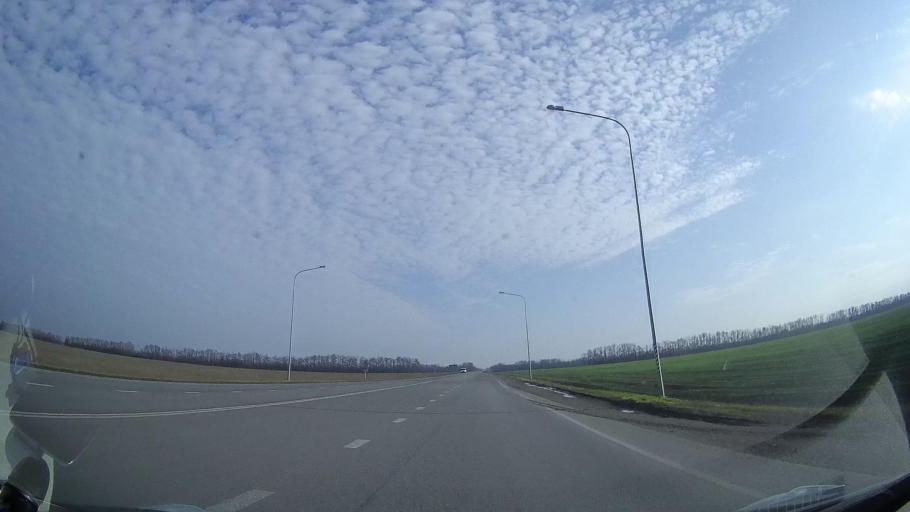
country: RU
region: Rostov
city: Tselina
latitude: 46.5262
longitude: 41.0850
